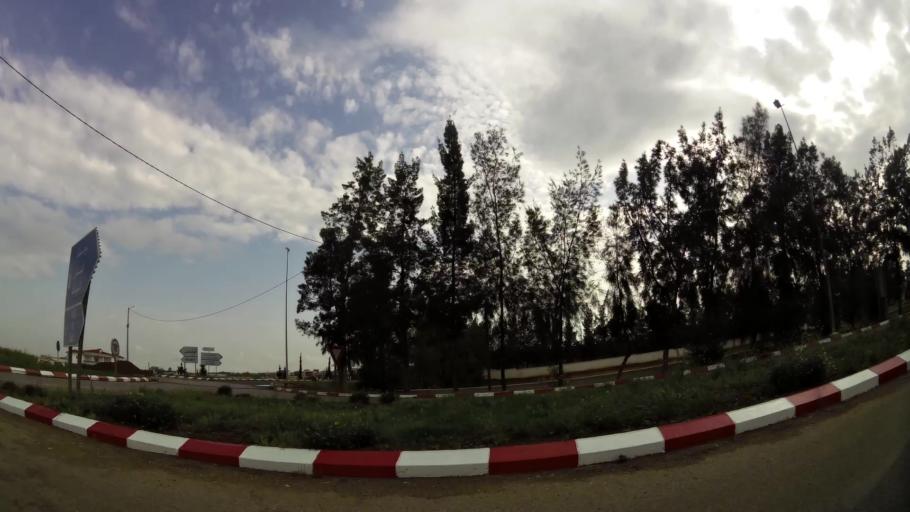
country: MA
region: Rabat-Sale-Zemmour-Zaer
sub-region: Khemisset
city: Khemisset
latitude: 33.8028
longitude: -6.0936
